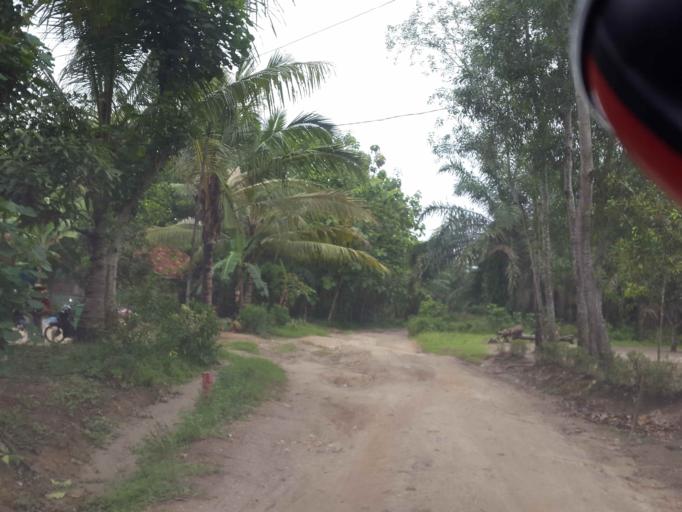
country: ID
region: Lampung
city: Natar
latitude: -5.2737
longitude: 105.2160
